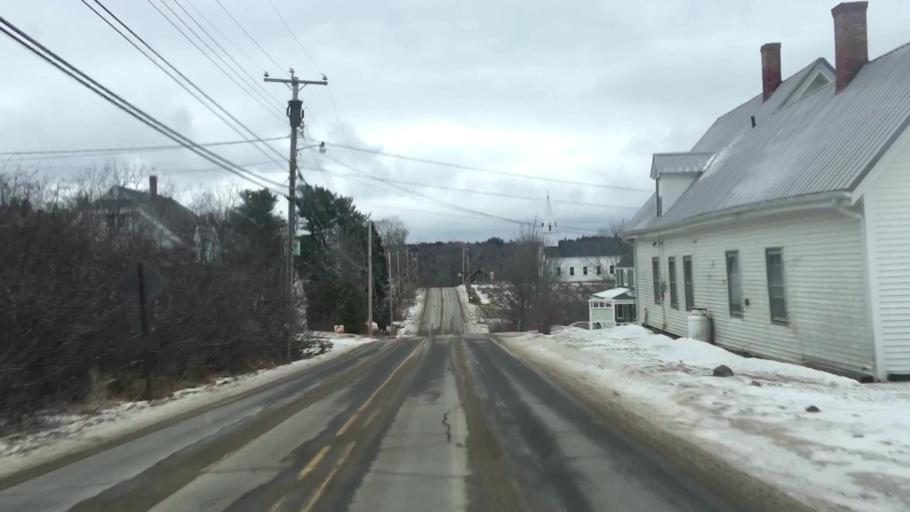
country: US
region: Maine
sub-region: Washington County
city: Machiasport
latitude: 44.6951
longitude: -67.3988
